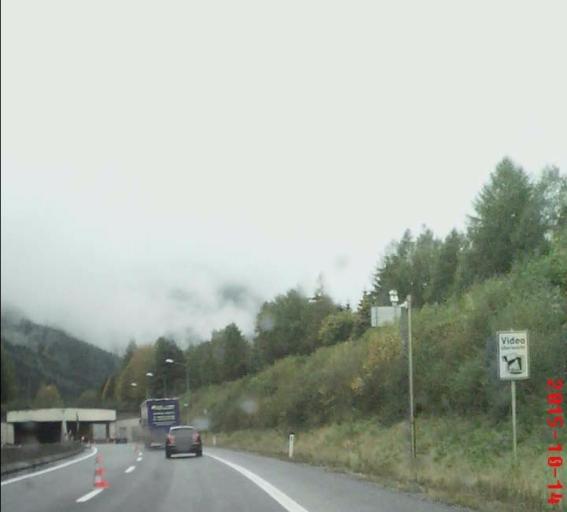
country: AT
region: Styria
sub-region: Politischer Bezirk Liezen
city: Rottenmann
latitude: 47.5236
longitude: 14.3655
